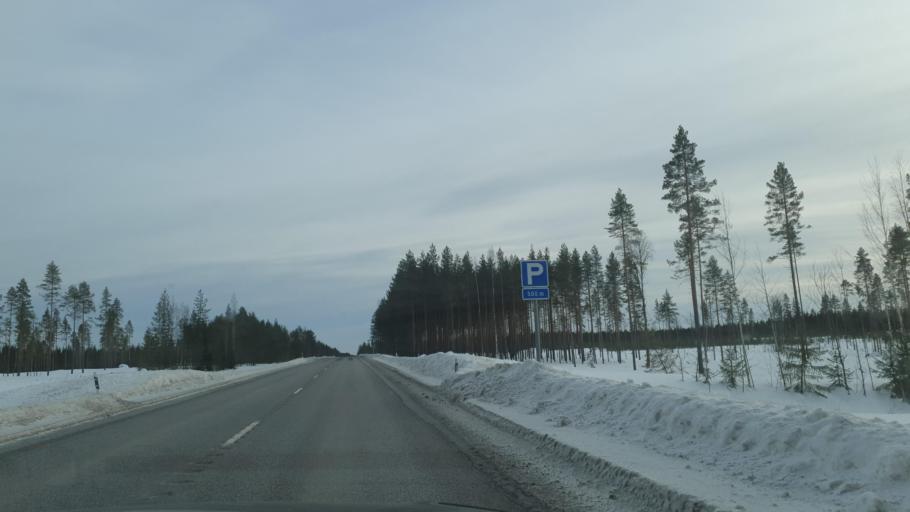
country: FI
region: Kainuu
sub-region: Kajaani
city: Vuolijoki
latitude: 64.5088
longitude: 27.2928
